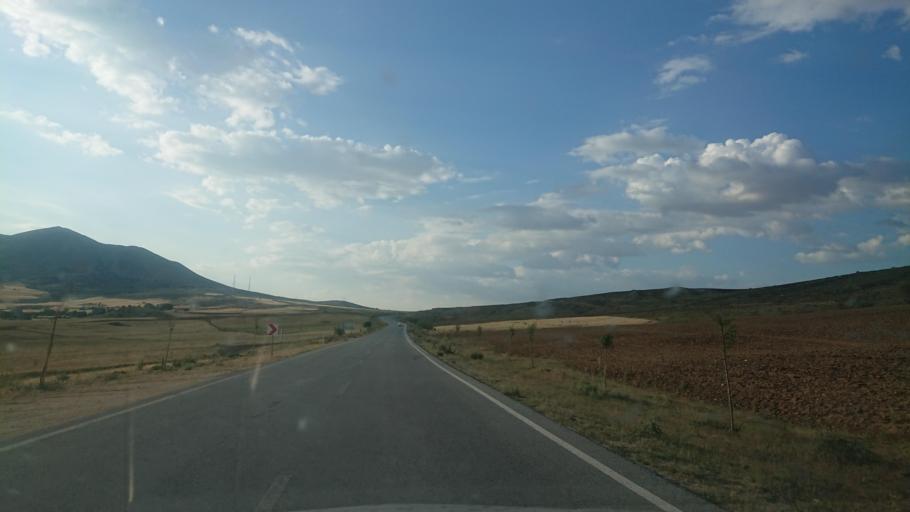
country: TR
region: Aksaray
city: Balci
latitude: 38.6022
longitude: 34.1030
